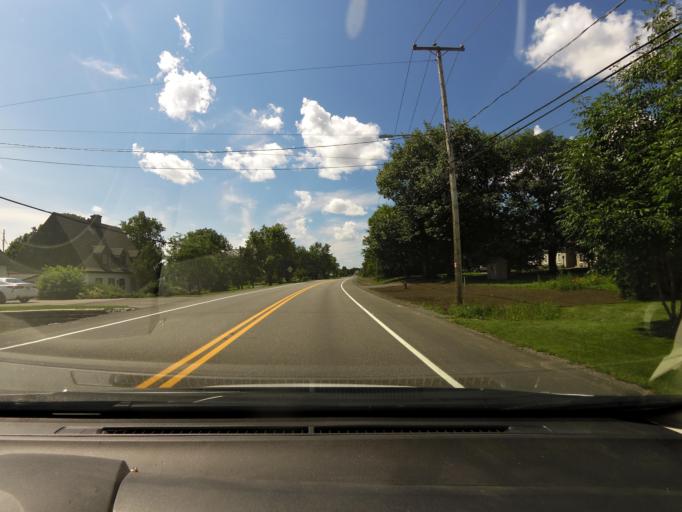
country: CA
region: Quebec
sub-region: Capitale-Nationale
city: Neuville
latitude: 46.7165
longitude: -71.5494
